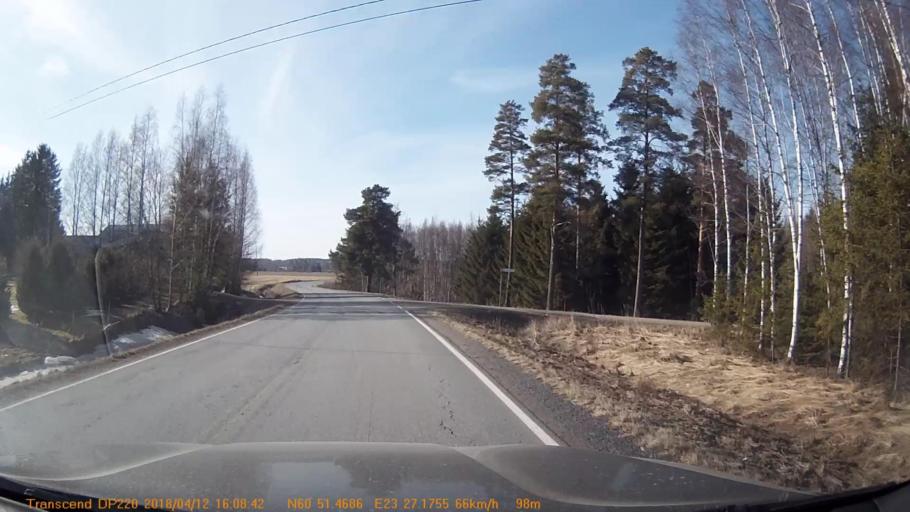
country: FI
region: Haeme
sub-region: Forssa
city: Jokioinen
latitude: 60.8576
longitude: 23.4535
